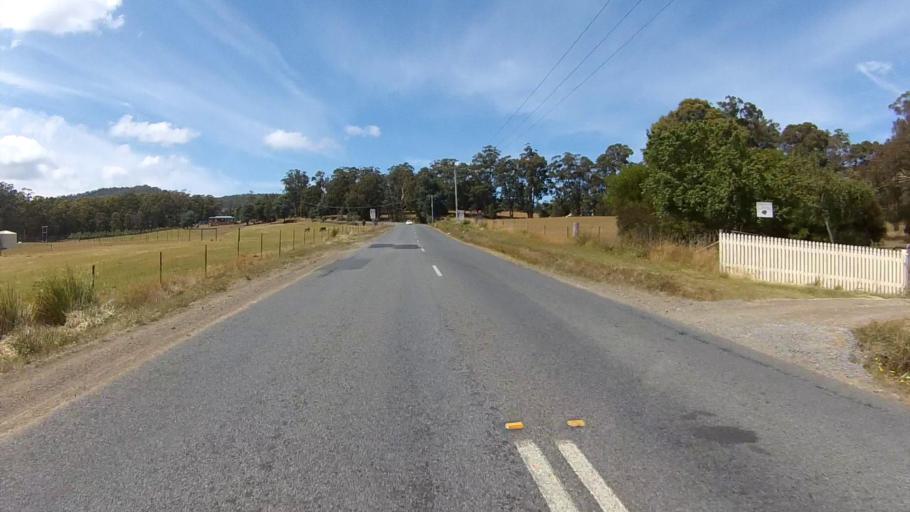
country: AU
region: Tasmania
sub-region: Huon Valley
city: Cygnet
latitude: -43.2121
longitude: 147.1164
